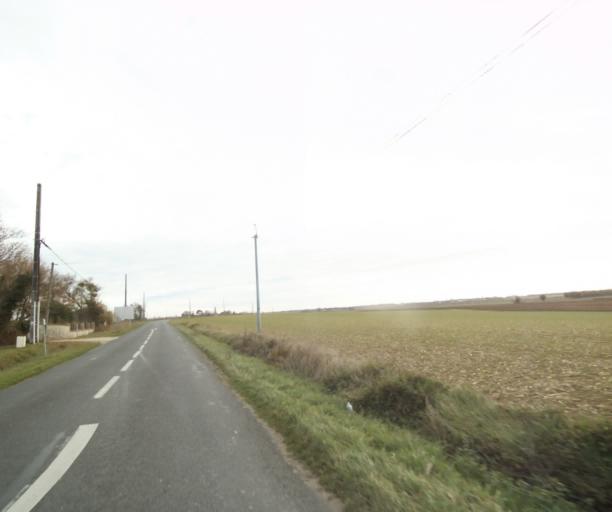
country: FR
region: Poitou-Charentes
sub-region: Departement de la Charente-Maritime
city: Corme-Royal
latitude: 45.7387
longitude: -0.8145
